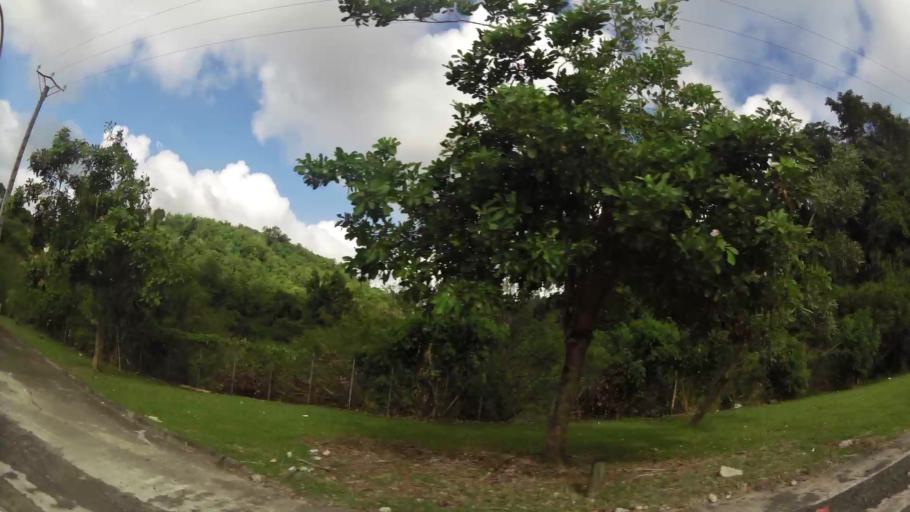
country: MQ
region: Martinique
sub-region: Martinique
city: Riviere-Pilote
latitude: 14.4694
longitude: -60.9063
